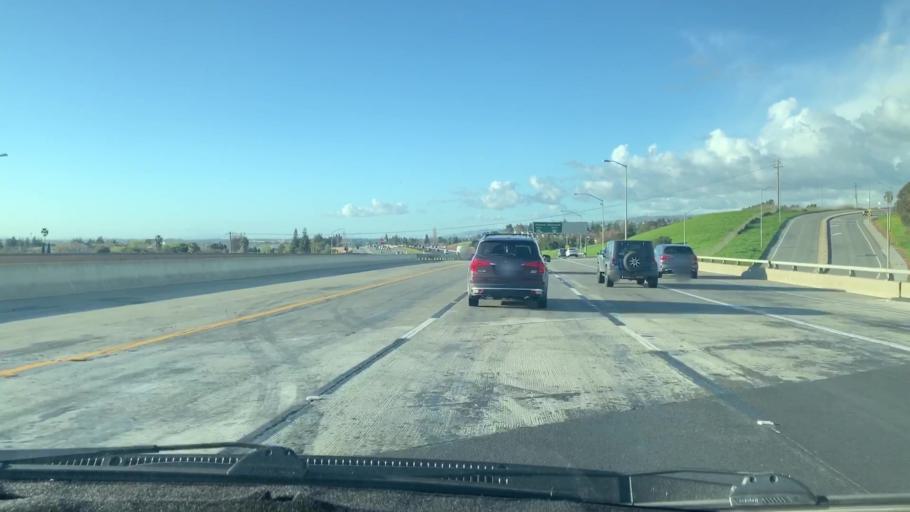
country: US
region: California
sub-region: Santa Clara County
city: Milpitas
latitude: 37.4905
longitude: -121.9180
